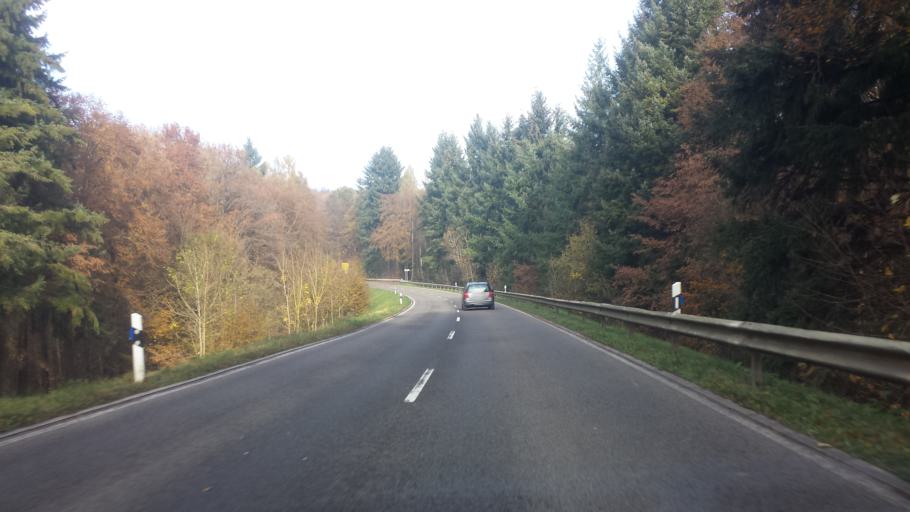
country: DE
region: Baden-Wuerttemberg
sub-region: Karlsruhe Region
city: Obrigheim
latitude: 49.3246
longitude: 9.0704
